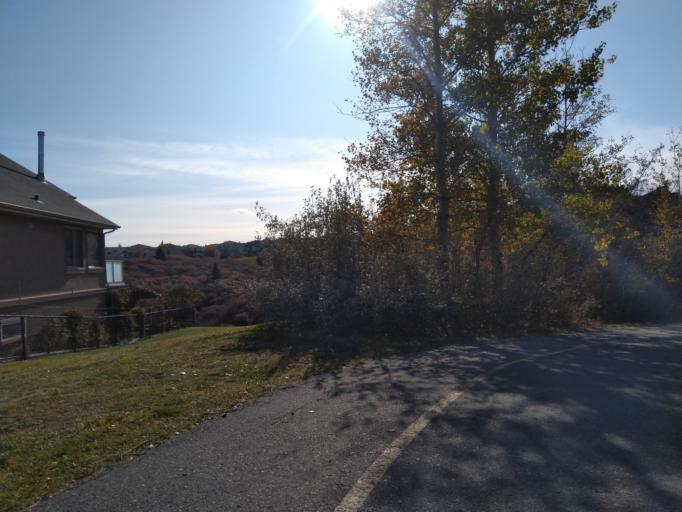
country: CA
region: Alberta
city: Calgary
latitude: 51.1368
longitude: -114.1457
